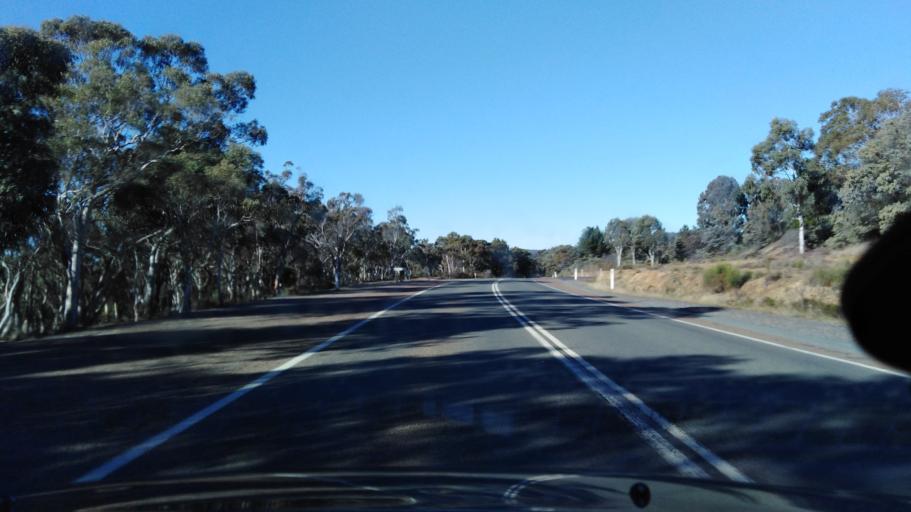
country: AU
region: New South Wales
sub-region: Palerang
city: Bungendore
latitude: -35.1872
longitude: 149.3238
